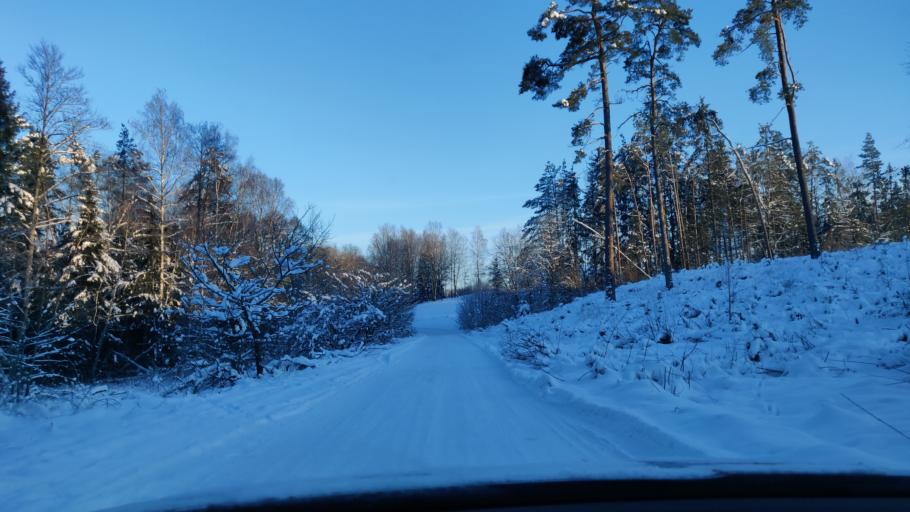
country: LT
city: Trakai
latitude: 54.6135
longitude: 24.9312
